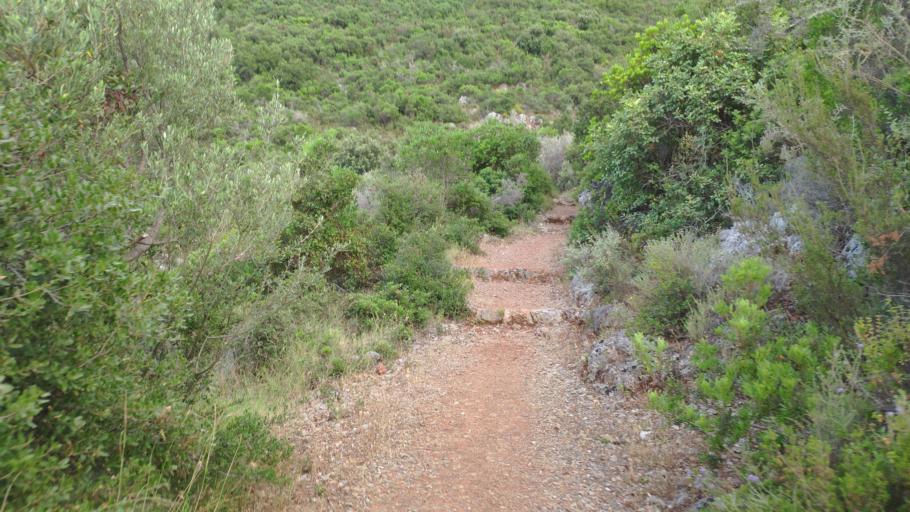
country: GR
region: Peloponnese
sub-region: Nomos Lakonias
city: Sykea
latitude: 36.9663
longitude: 23.0005
